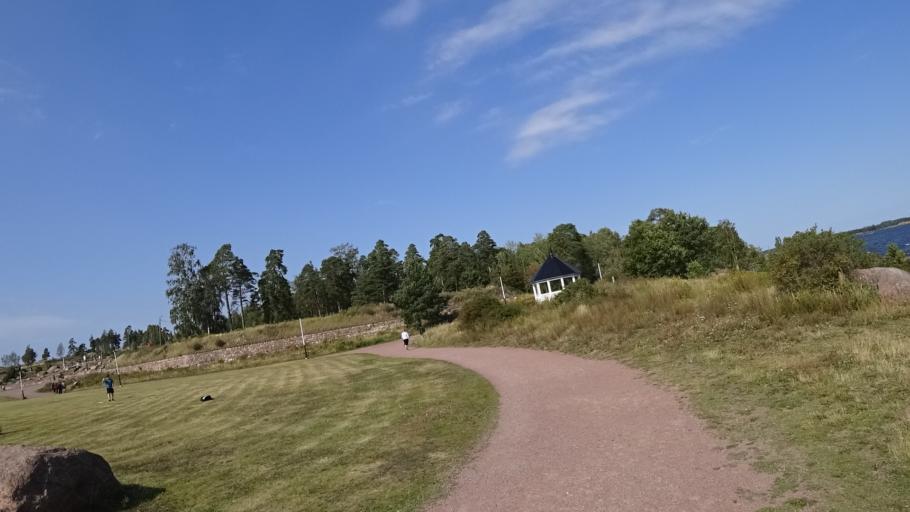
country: FI
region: Kymenlaakso
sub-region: Kotka-Hamina
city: Kotka
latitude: 60.4465
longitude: 26.9423
